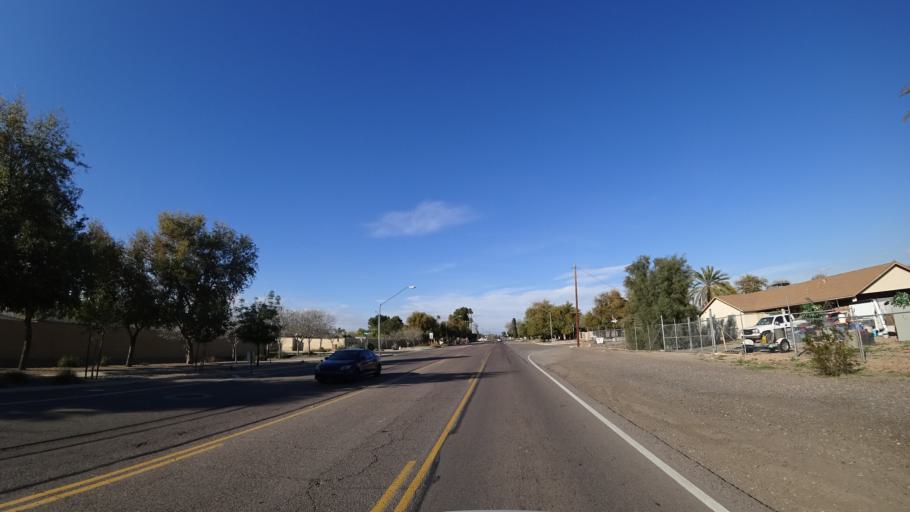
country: US
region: Arizona
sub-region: Maricopa County
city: Peoria
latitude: 33.5471
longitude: -112.2378
